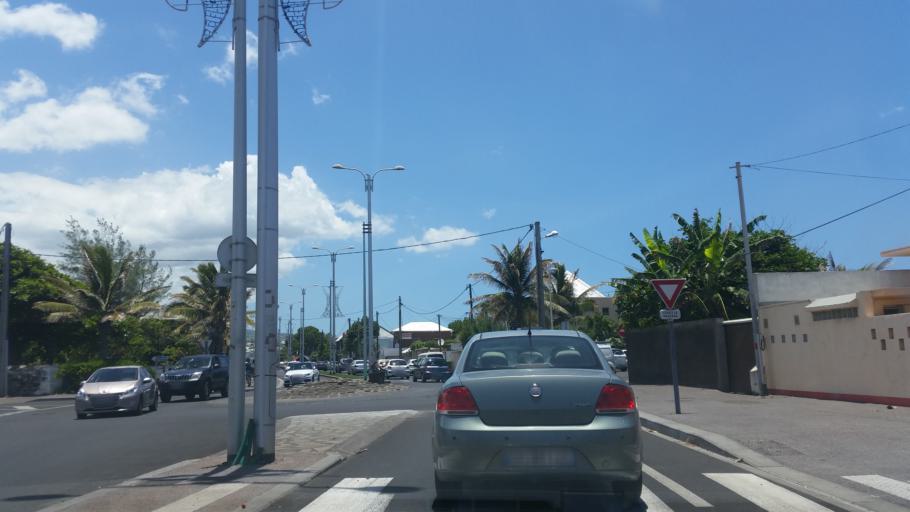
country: RE
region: Reunion
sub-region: Reunion
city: Saint-Pierre
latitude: -21.3435
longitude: 55.4678
